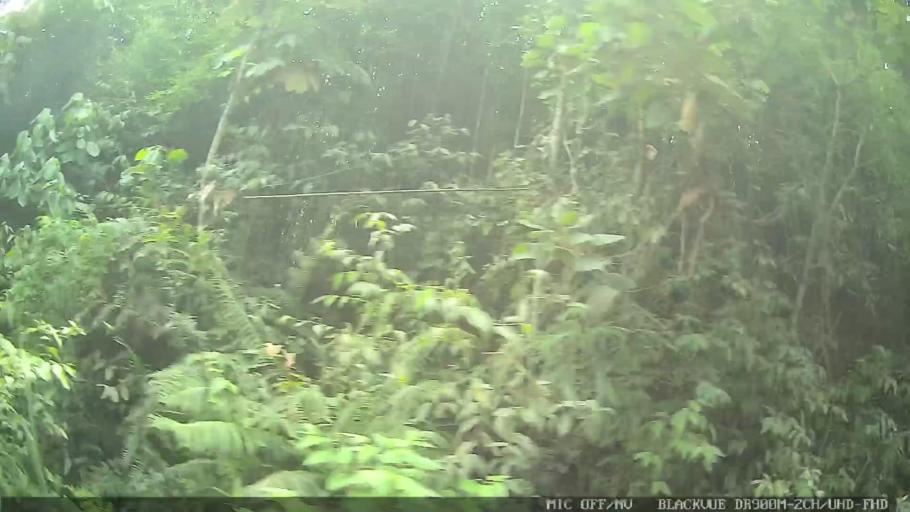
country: BR
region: Sao Paulo
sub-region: Santa Isabel
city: Santa Isabel
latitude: -23.3784
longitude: -46.2380
